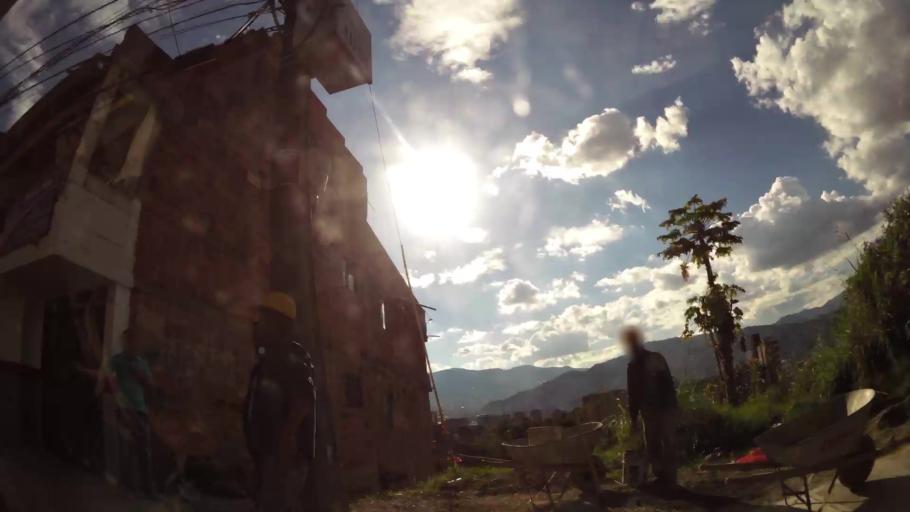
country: CO
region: Antioquia
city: Envigado
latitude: 6.1779
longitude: -75.5786
